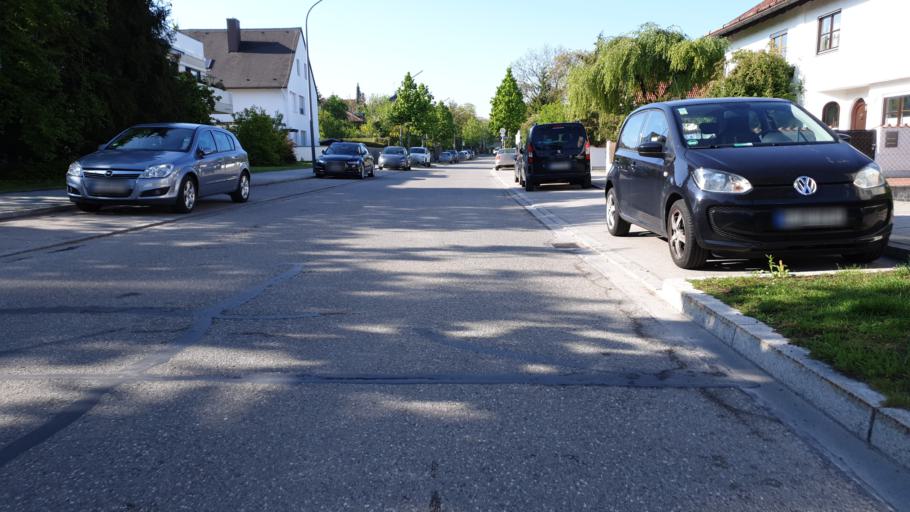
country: DE
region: Bavaria
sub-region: Upper Bavaria
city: Pasing
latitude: 48.1700
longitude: 11.4647
